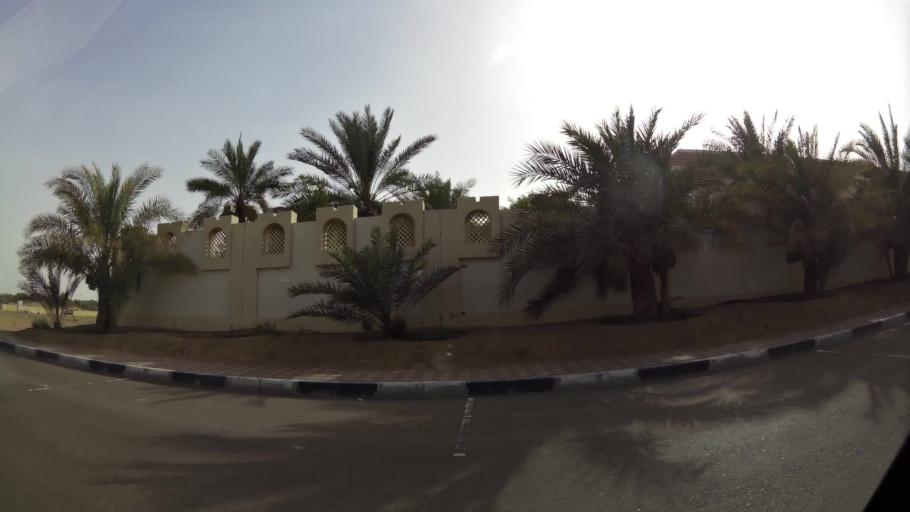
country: AE
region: Abu Dhabi
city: Al Ain
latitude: 24.1903
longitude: 55.6030
